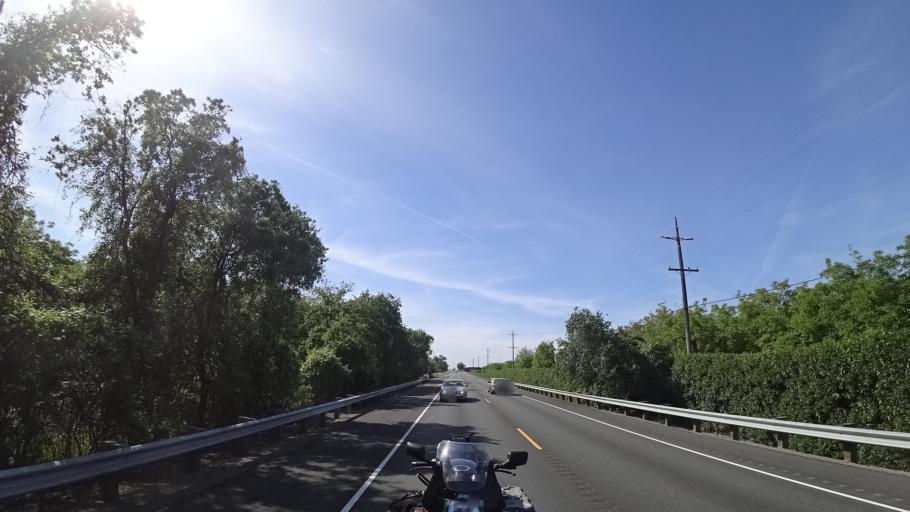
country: US
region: California
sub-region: Glenn County
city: Hamilton City
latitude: 39.8826
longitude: -121.9753
